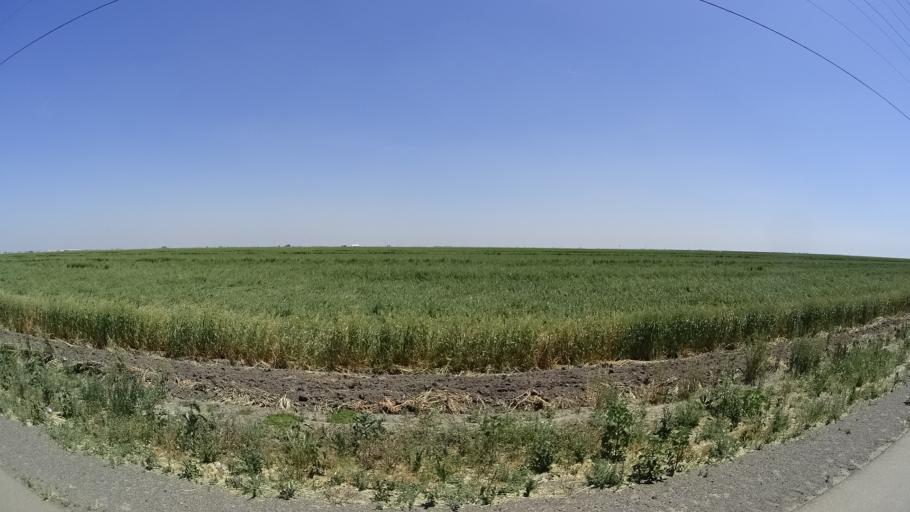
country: US
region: California
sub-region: Kings County
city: Corcoran
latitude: 36.1560
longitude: -119.6458
